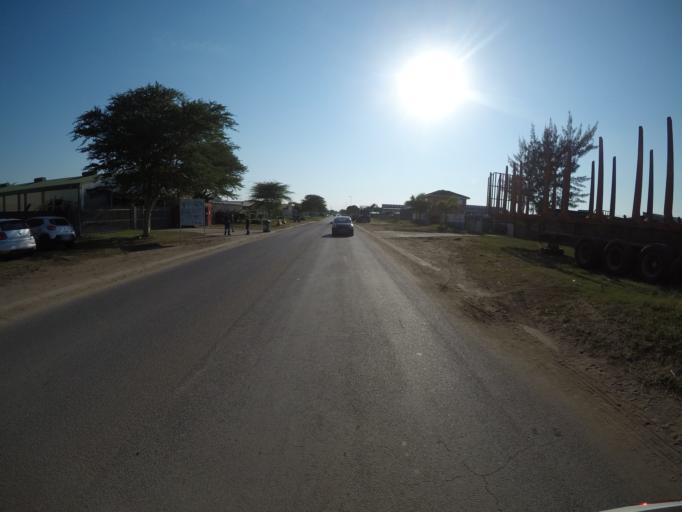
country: ZA
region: KwaZulu-Natal
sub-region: uThungulu District Municipality
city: Richards Bay
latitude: -28.7479
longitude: 32.0341
